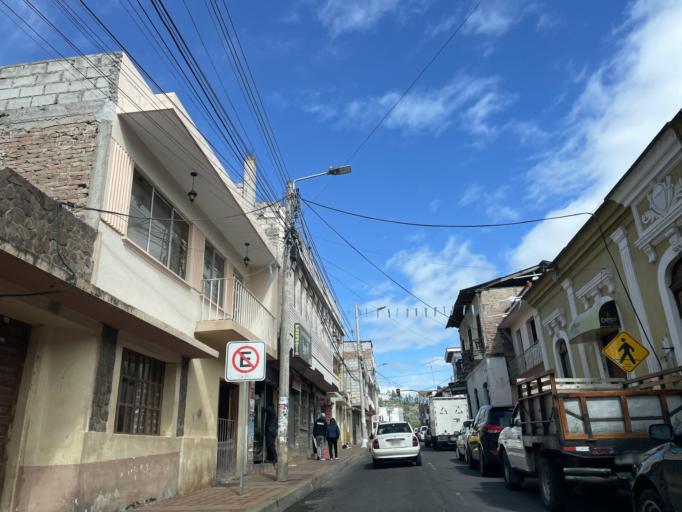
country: EC
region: Chimborazo
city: Guano
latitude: -1.6074
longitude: -78.6437
